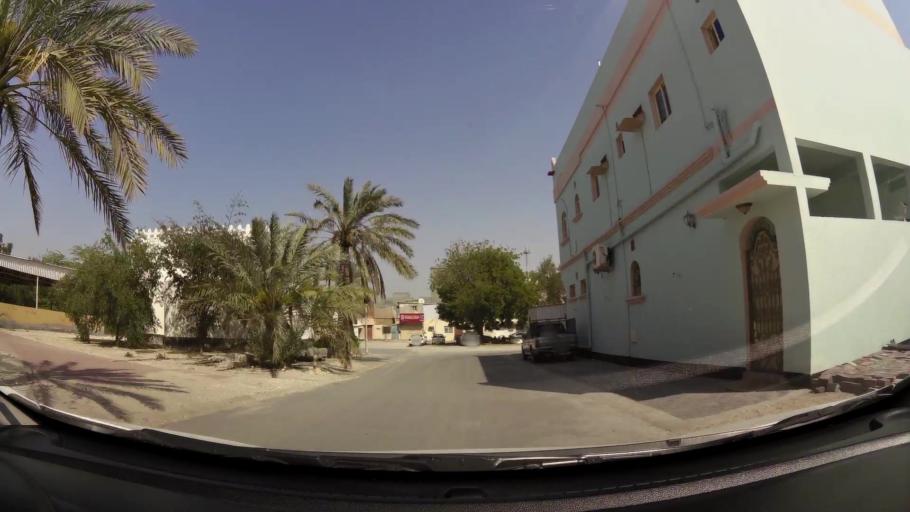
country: BH
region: Manama
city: Jidd Hafs
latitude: 26.1972
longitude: 50.4641
